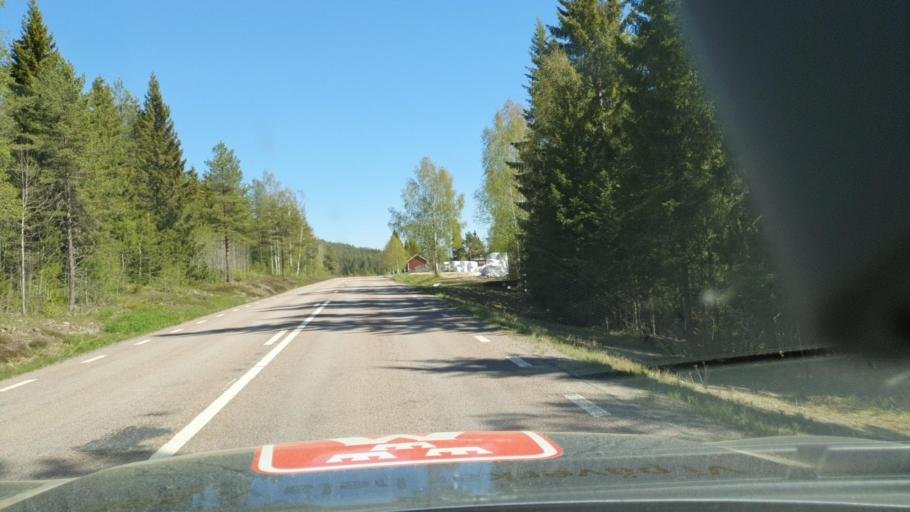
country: SE
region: Vaesternorrland
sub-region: OErnskoeldsviks Kommun
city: Ornskoldsvik
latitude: 63.4136
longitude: 18.6186
